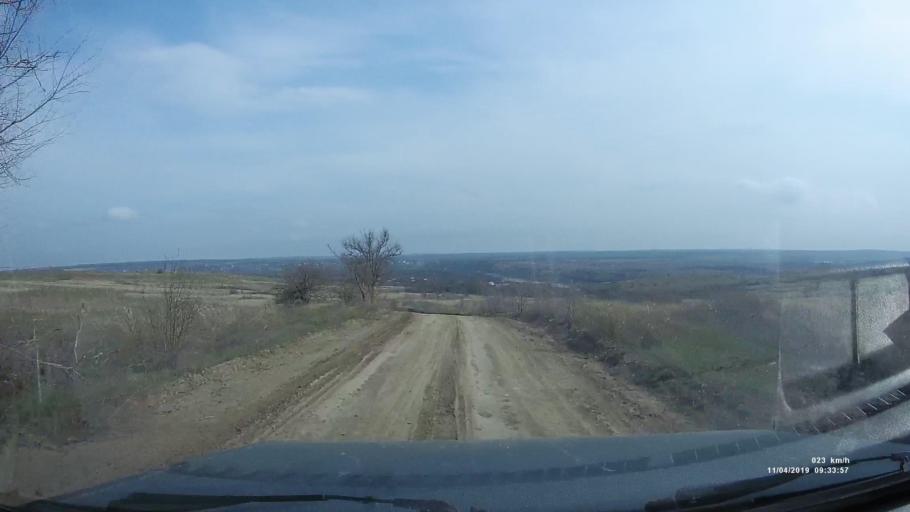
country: RU
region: Rostov
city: Staraya Stanitsa
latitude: 48.2676
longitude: 40.3682
